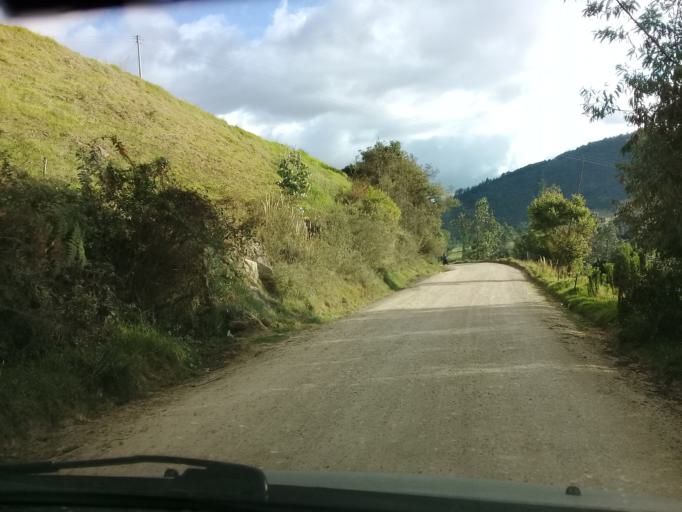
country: CO
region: Cundinamarca
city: Villapinzon
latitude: 5.2219
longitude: -73.6445
